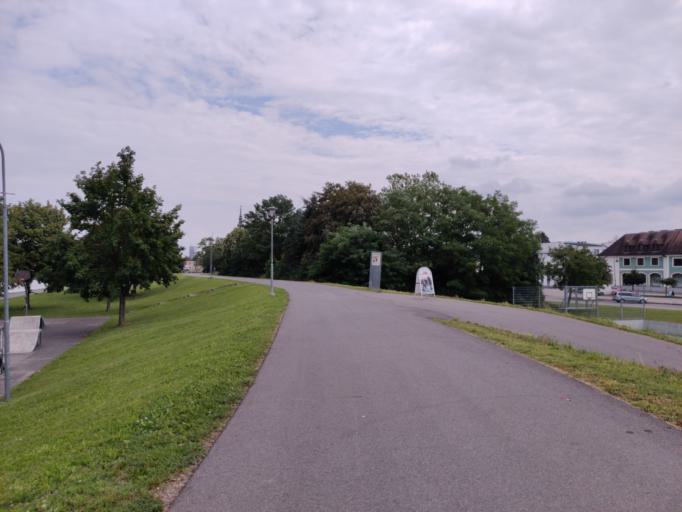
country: AT
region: Lower Austria
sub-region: Politischer Bezirk Melk
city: Klein-Poechlarn
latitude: 48.2127
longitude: 15.2063
